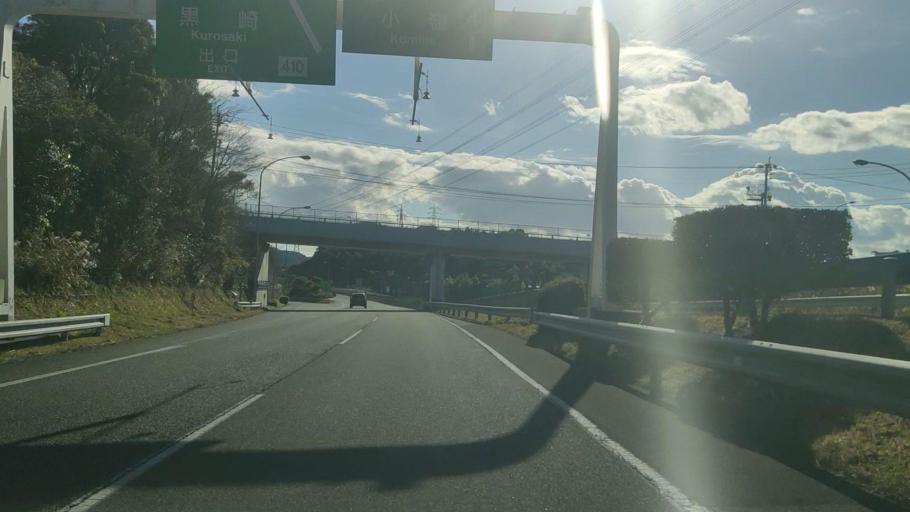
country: JP
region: Fukuoka
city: Kitakyushu
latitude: 33.8433
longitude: 130.7658
